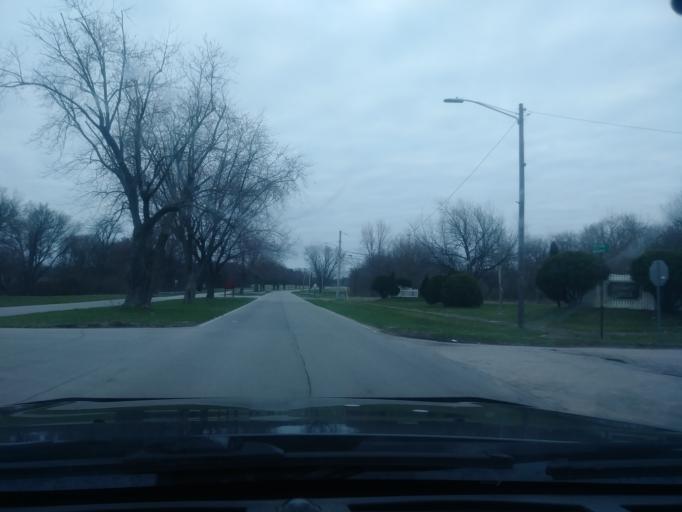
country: US
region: Indiana
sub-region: LaPorte County
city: Kingsford Heights
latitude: 41.4830
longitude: -86.6888
